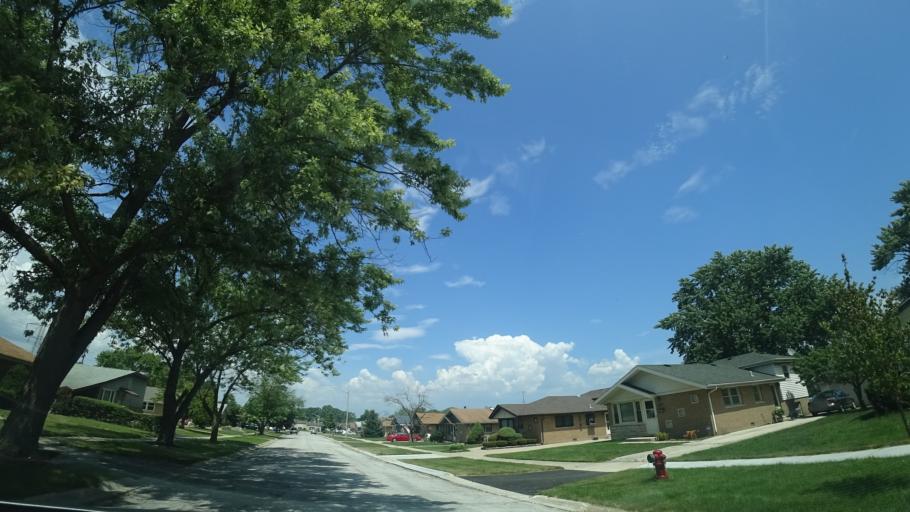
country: US
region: Illinois
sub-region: Cook County
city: Alsip
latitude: 41.6640
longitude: -87.7260
